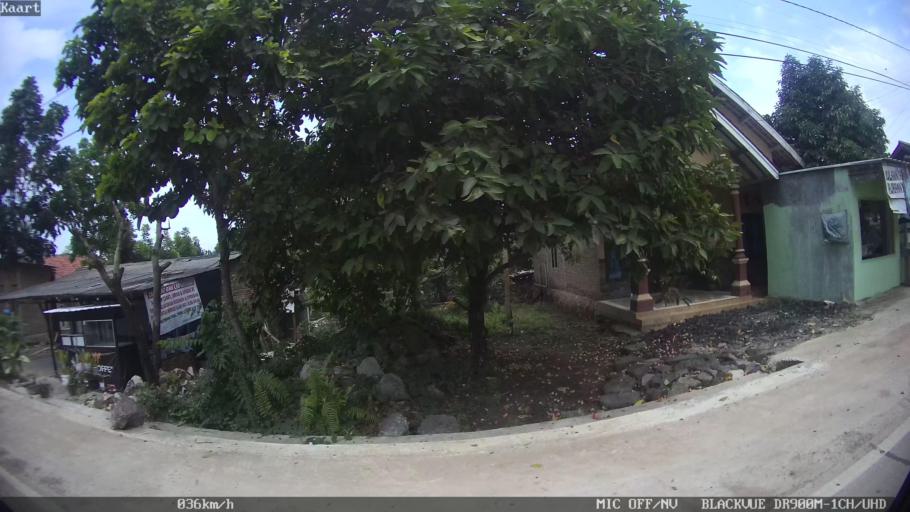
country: ID
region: Lampung
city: Kedaton
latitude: -5.3625
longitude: 105.3083
